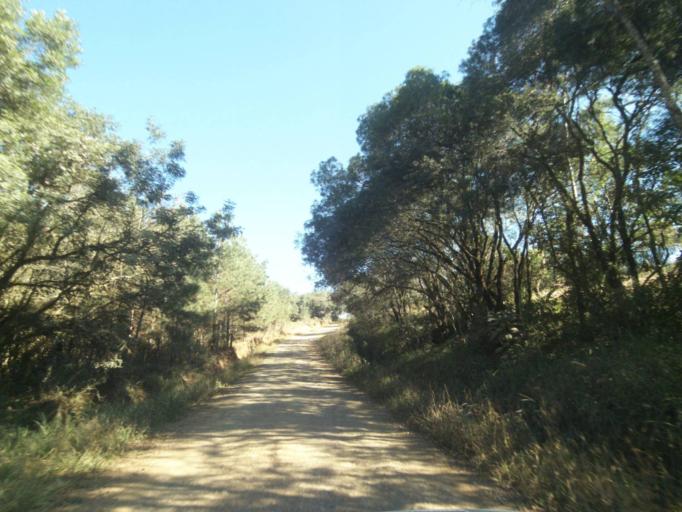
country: BR
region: Parana
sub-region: Tibagi
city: Tibagi
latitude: -24.5469
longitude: -50.5118
